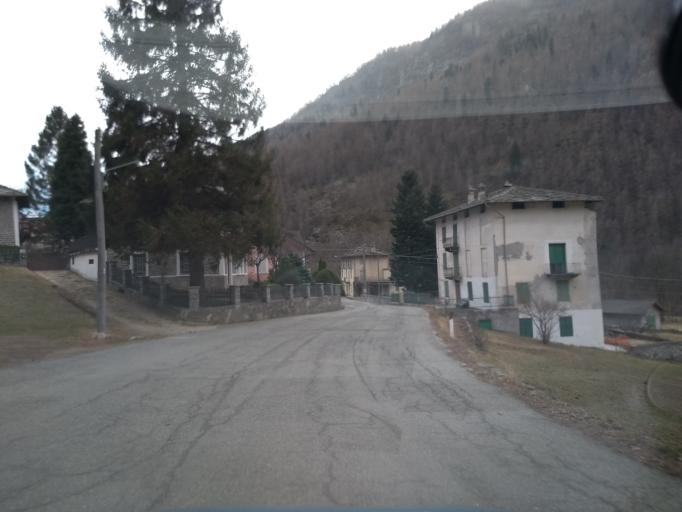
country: IT
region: Piedmont
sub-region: Provincia di Torino
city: Chialamberto
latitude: 45.3690
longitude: 7.3036
